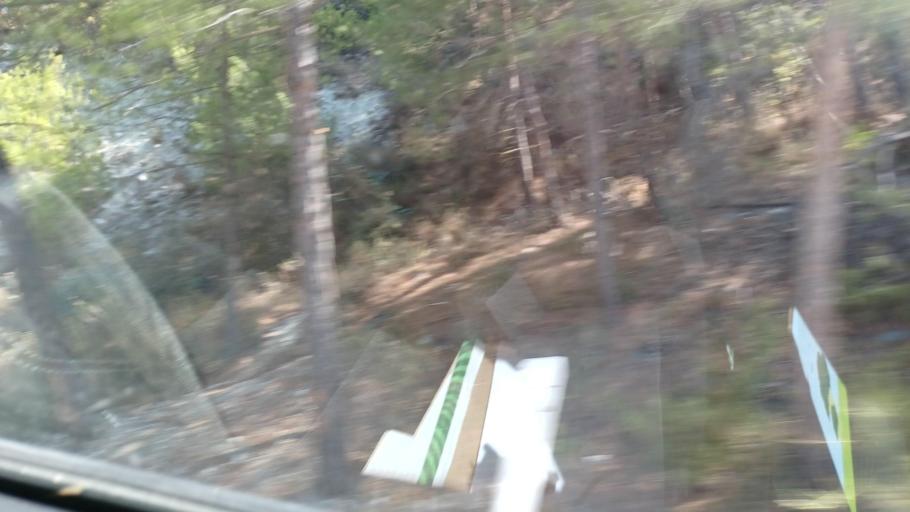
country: CY
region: Pafos
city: Mesogi
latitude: 34.9140
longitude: 32.6284
